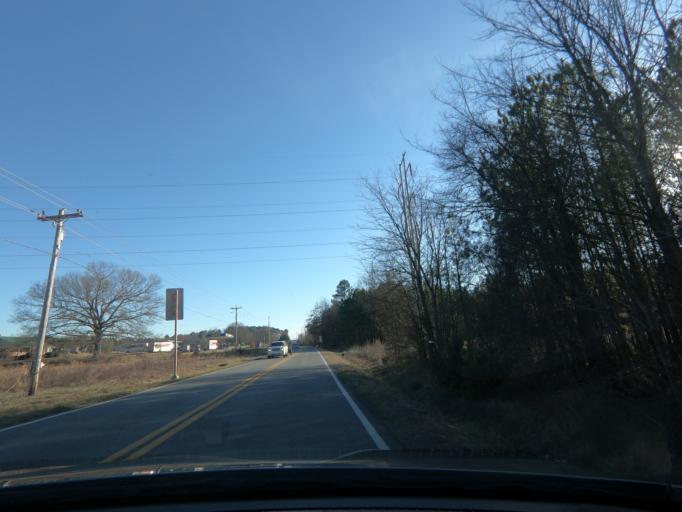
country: US
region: Georgia
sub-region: Gordon County
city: Calhoun
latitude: 34.4531
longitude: -84.9147
